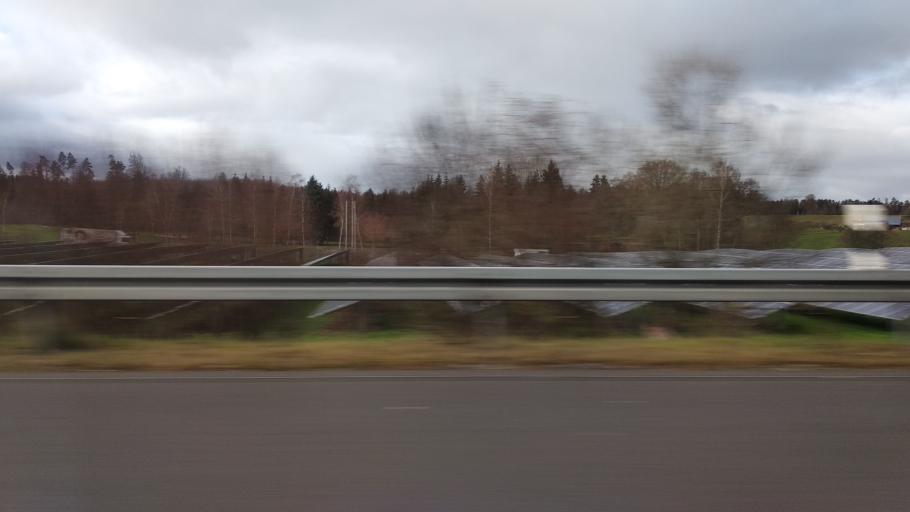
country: DE
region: Bavaria
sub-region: Swabia
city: Weissensberg
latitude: 47.6011
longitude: 9.7320
